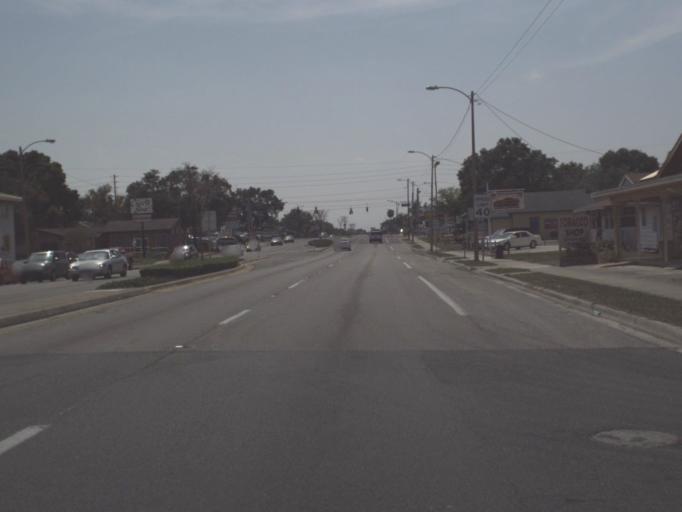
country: US
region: Florida
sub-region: Lake County
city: Eustis
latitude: 28.8438
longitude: -81.6856
